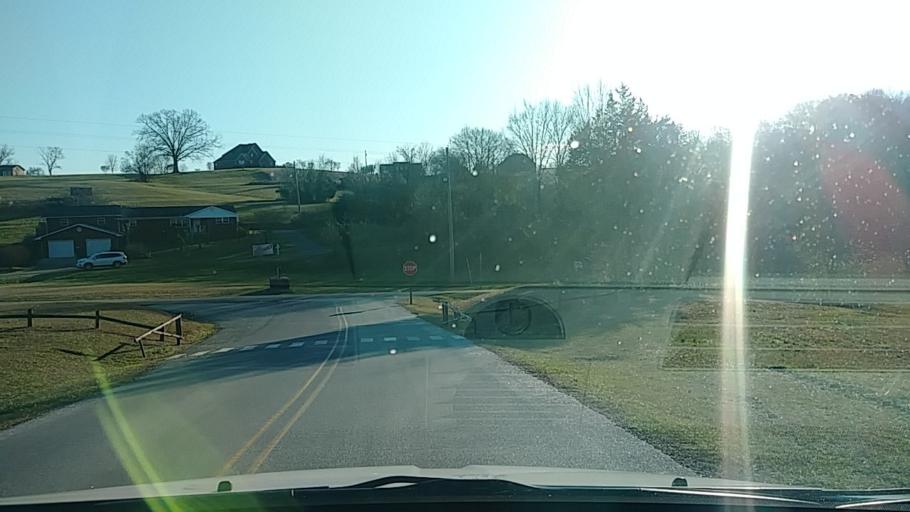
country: US
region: Tennessee
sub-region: Hamblen County
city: Morristown
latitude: 36.2059
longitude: -83.4072
